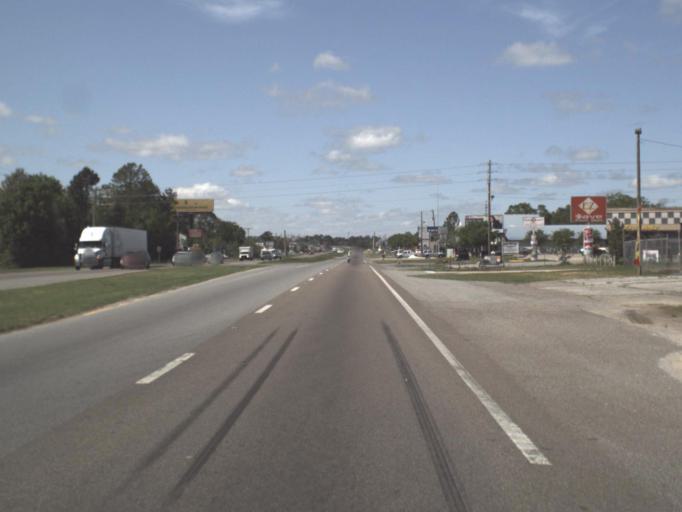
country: US
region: Florida
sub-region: Escambia County
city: Ensley
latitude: 30.5189
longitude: -87.2726
